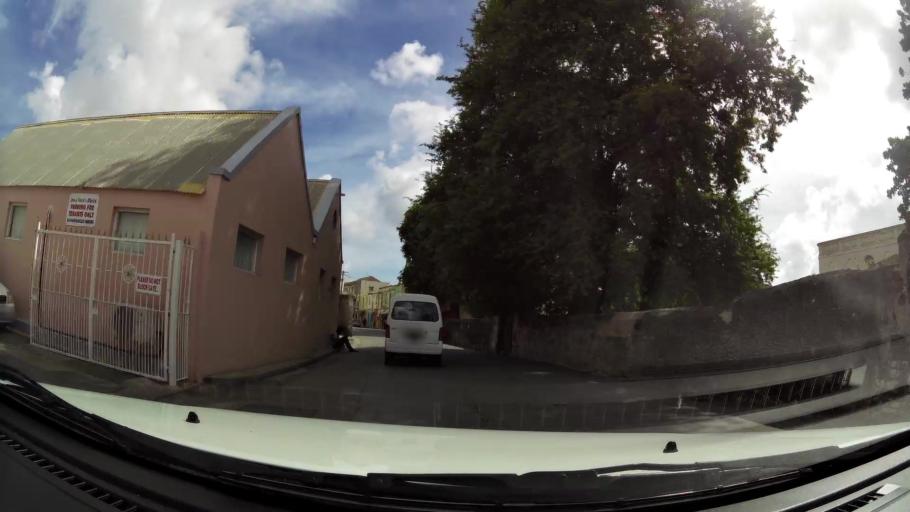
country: BB
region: Saint Michael
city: Bridgetown
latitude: 13.0997
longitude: -59.6150
